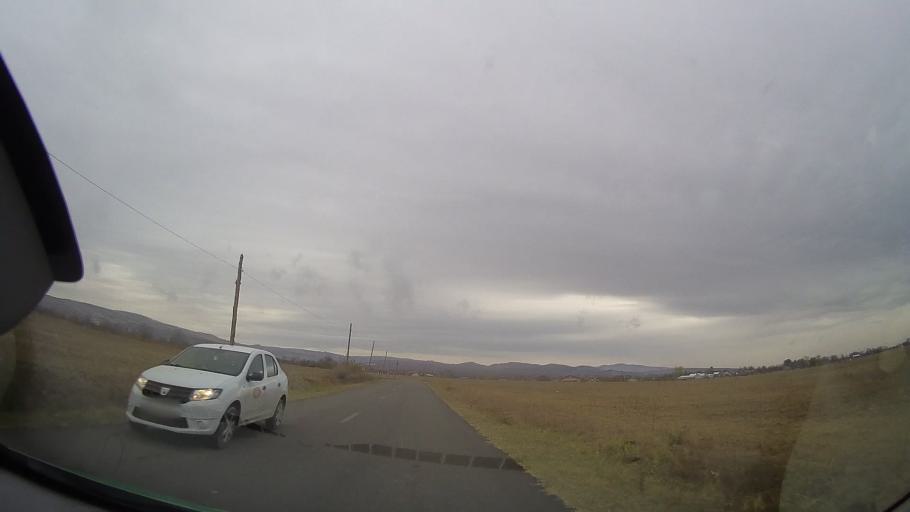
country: RO
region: Prahova
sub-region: Comuna Vadu Sapat
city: Vadu Sapat
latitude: 45.0239
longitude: 26.3819
